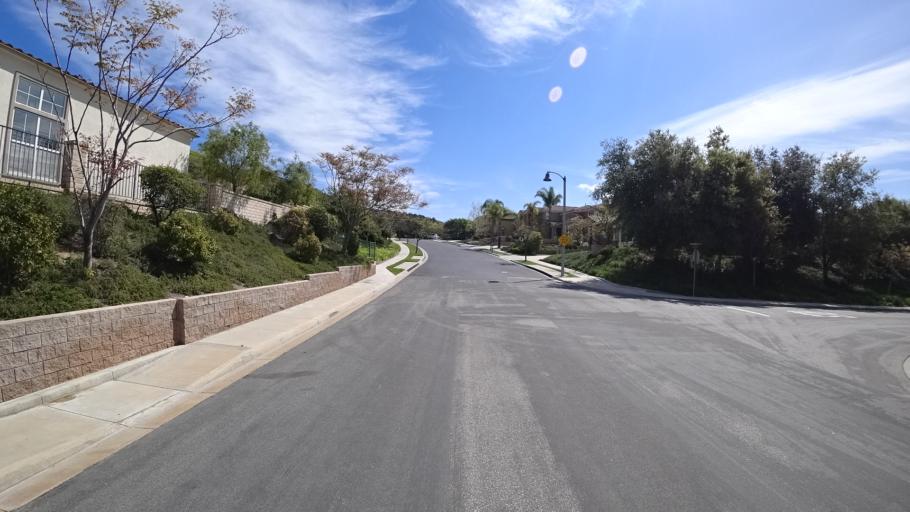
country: US
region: California
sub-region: Ventura County
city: Thousand Oaks
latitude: 34.2238
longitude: -118.8304
